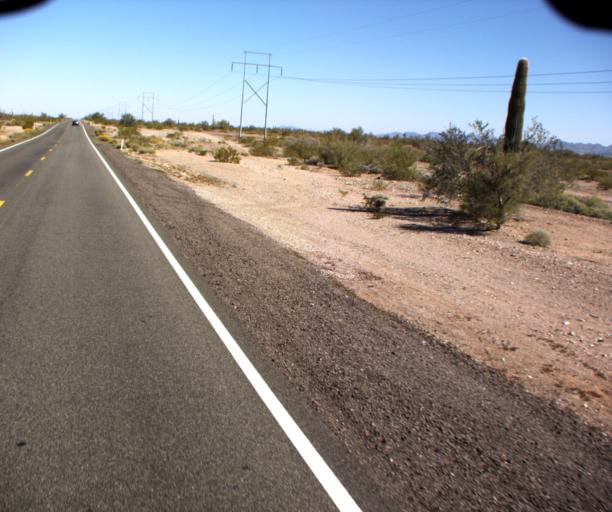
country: US
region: Arizona
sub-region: La Paz County
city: Quartzsite
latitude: 33.5493
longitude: -114.2170
